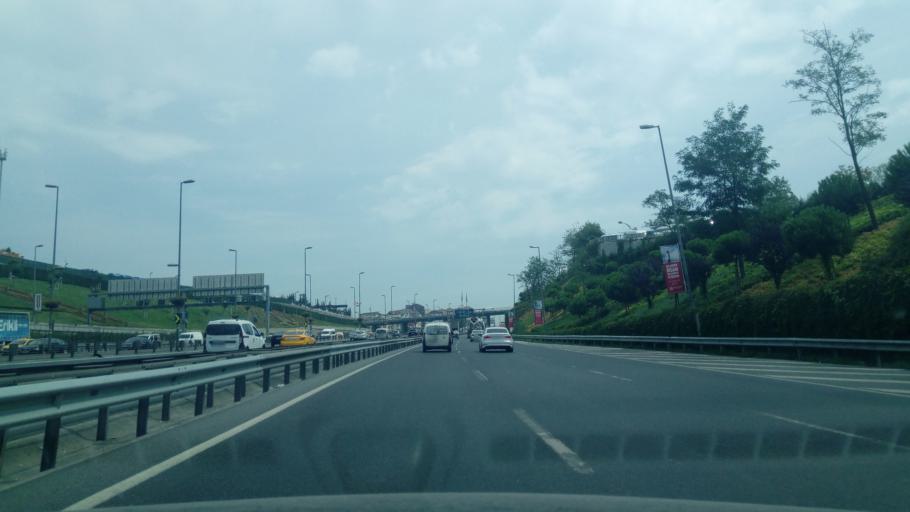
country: TR
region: Istanbul
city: Istanbul
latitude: 41.0499
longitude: 28.9480
